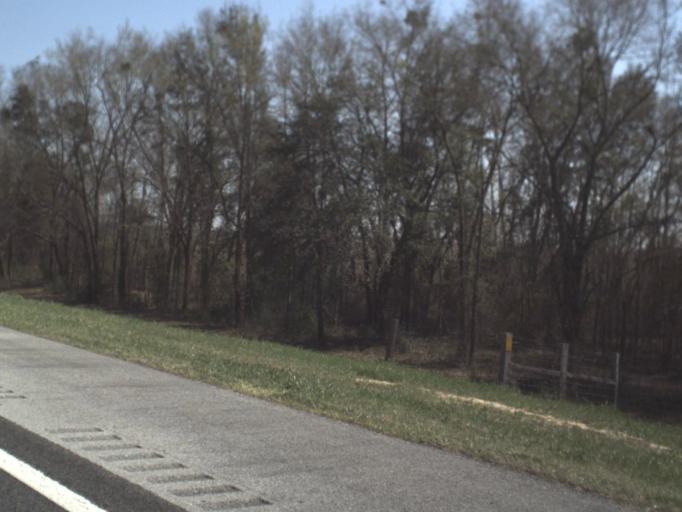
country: US
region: Florida
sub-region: Jackson County
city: Marianna
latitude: 30.6843
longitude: -85.1057
